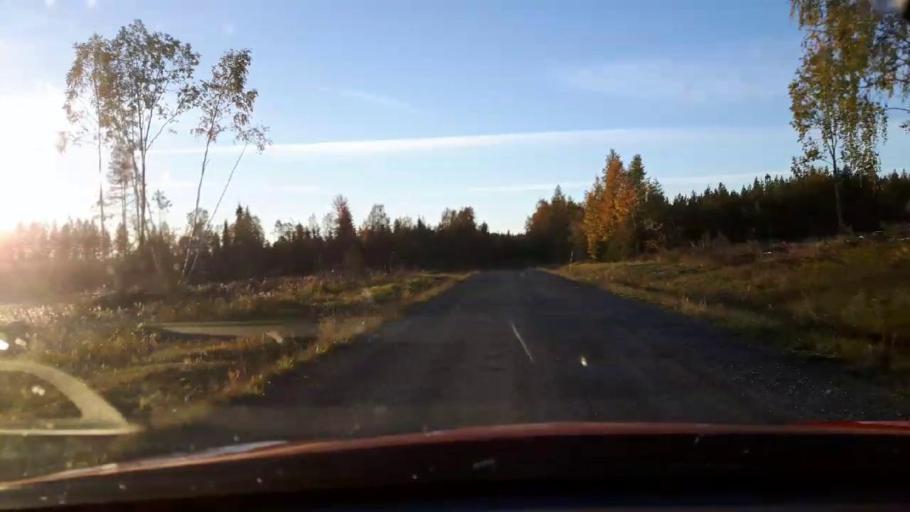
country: SE
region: Jaemtland
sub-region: Krokoms Kommun
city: Krokom
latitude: 63.4407
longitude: 14.5971
